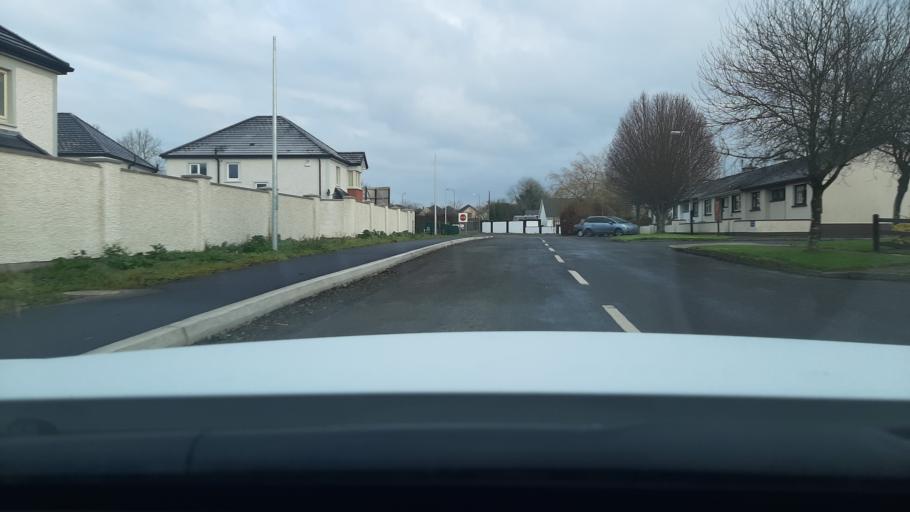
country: IE
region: Leinster
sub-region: Kildare
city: Rathangan
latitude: 53.2234
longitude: -7.0027
